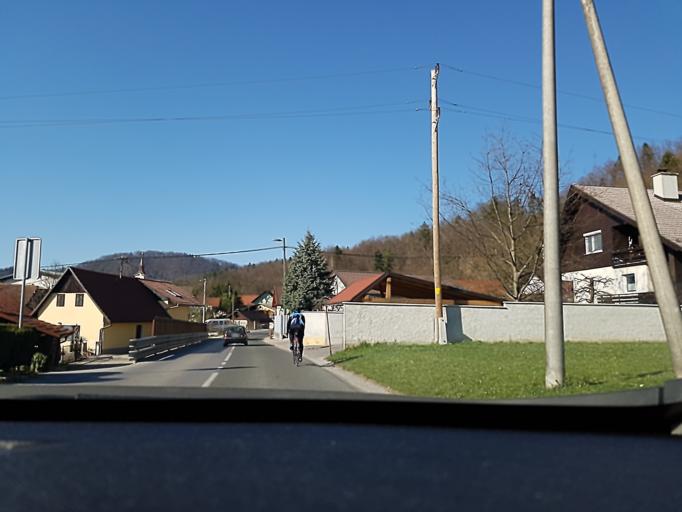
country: SI
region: Trzin
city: Trzin
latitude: 46.1209
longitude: 14.5038
